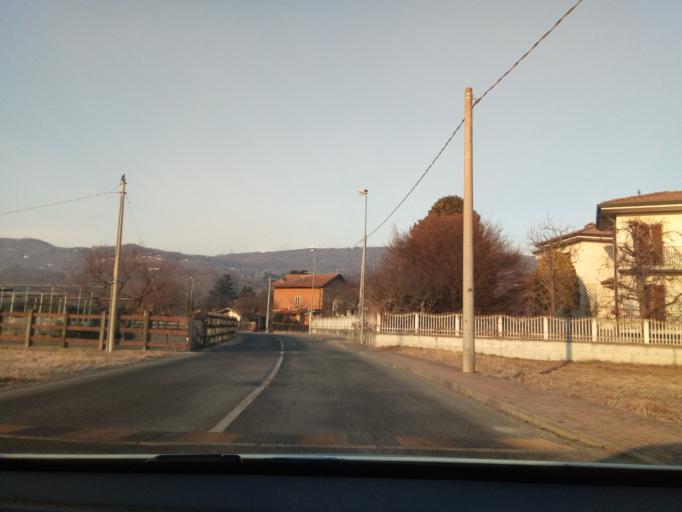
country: IT
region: Piedmont
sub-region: Provincia di Torino
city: Fiorano Canavese
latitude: 45.4676
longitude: 7.8392
